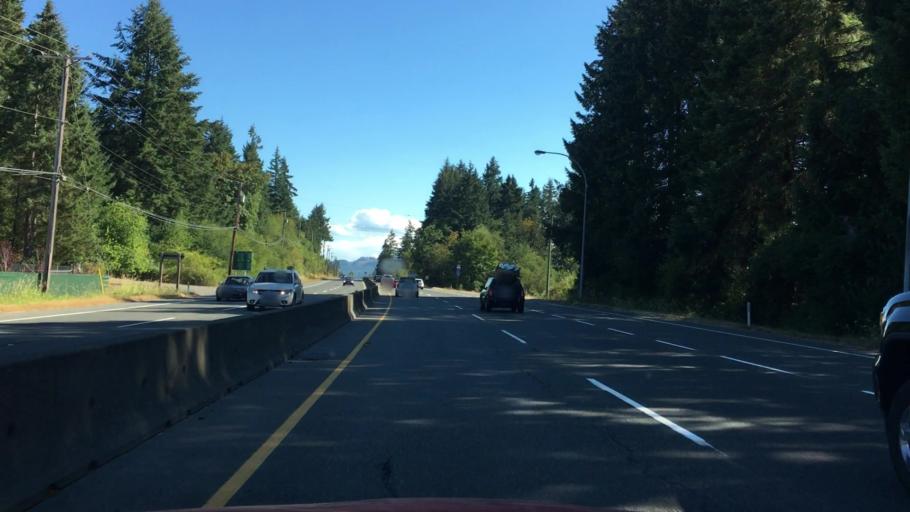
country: CA
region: British Columbia
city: Duncan
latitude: 48.8128
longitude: -123.7180
